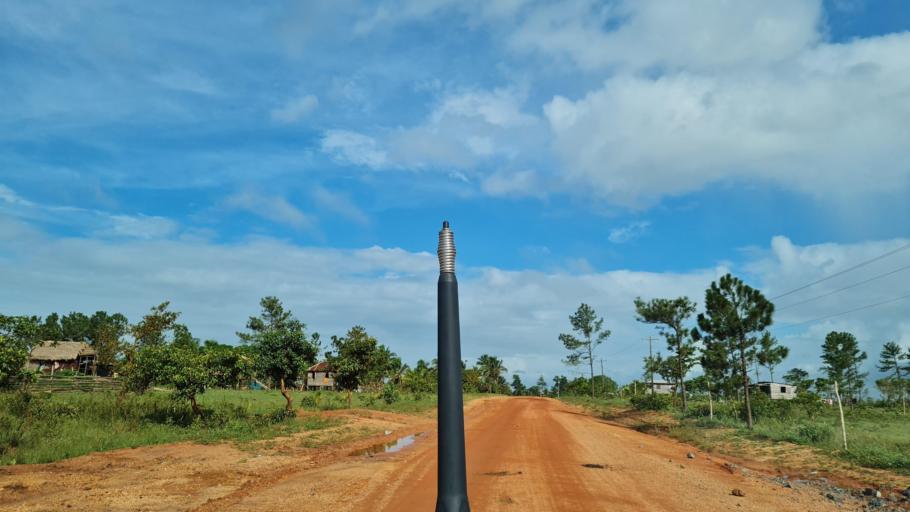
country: NI
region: Atlantico Norte (RAAN)
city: Puerto Cabezas
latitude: 14.1625
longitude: -83.5212
